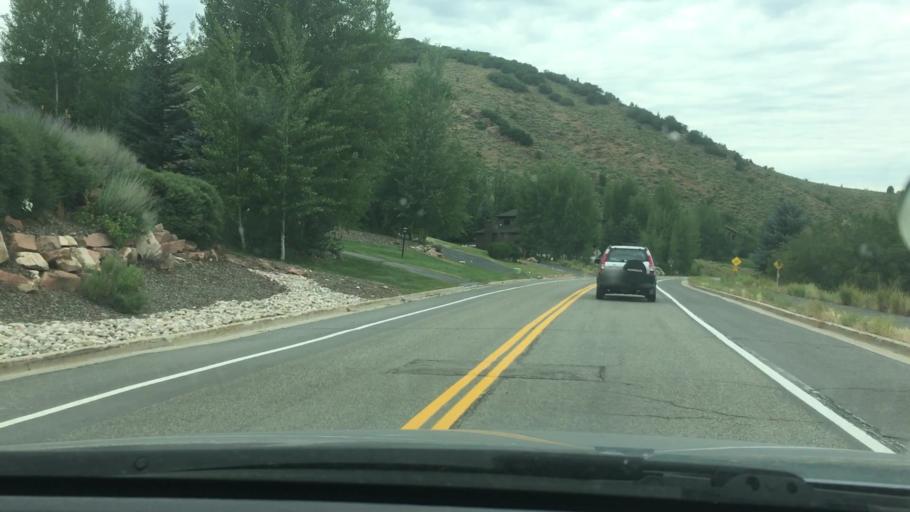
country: US
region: Utah
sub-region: Summit County
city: Summit Park
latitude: 40.7643
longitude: -111.5814
